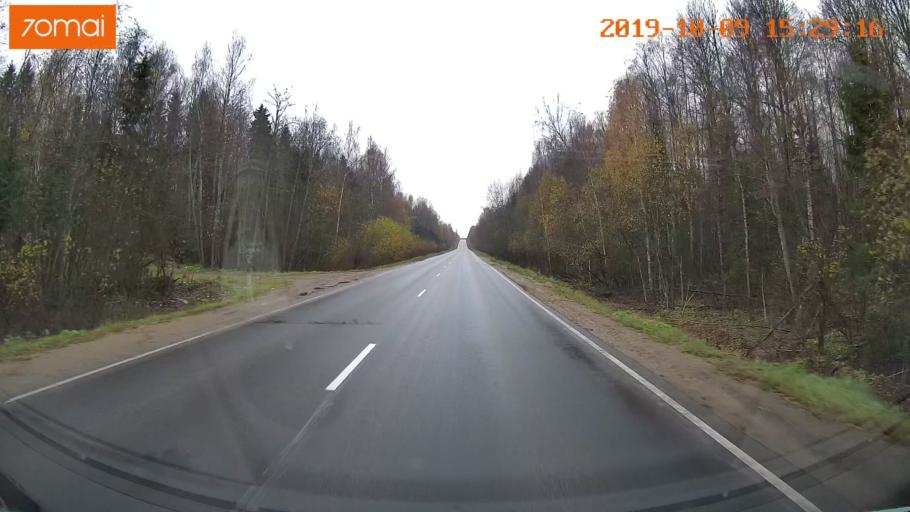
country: RU
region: Kostroma
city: Susanino
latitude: 57.9935
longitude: 41.3458
